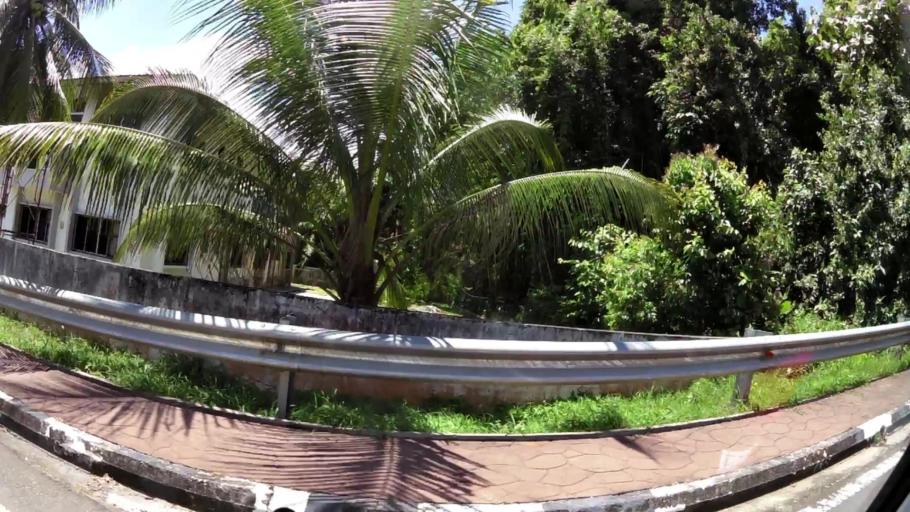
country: BN
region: Brunei and Muara
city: Bandar Seri Begawan
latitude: 4.9416
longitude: 114.9609
